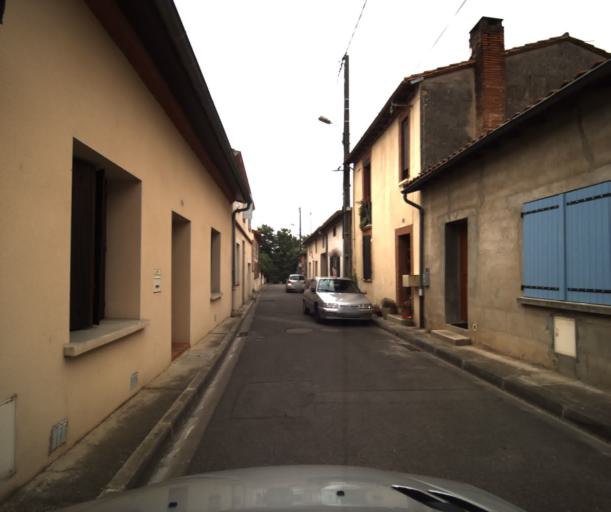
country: FR
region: Midi-Pyrenees
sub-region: Departement de la Haute-Garonne
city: Portet-sur-Garonne
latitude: 43.5206
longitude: 1.4063
